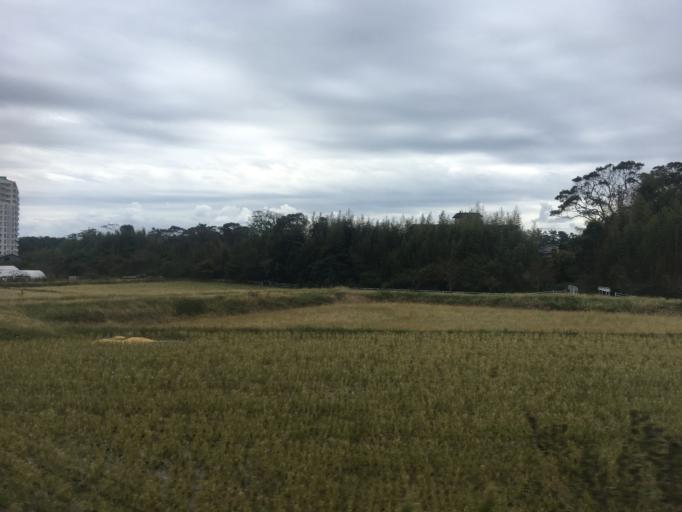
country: JP
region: Chiba
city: Kawaguchi
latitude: 35.1211
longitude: 140.1193
